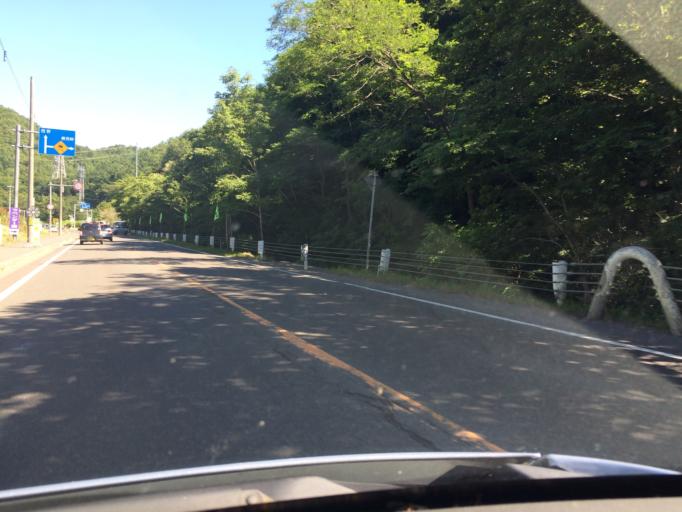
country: JP
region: Hokkaido
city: Sapporo
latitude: 43.0262
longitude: 141.2897
